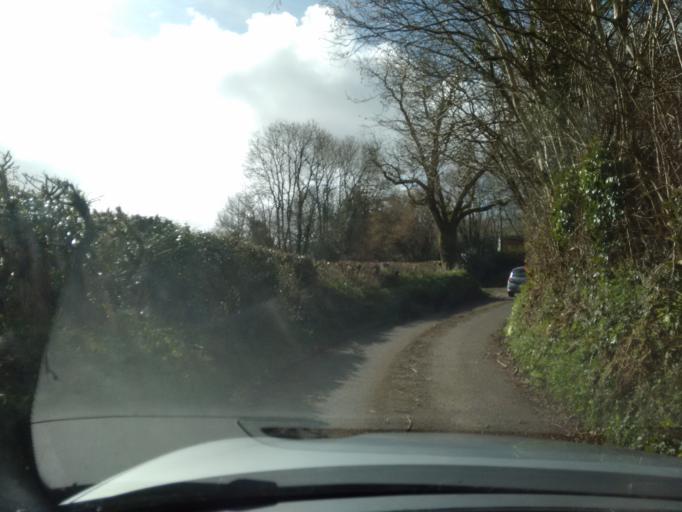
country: GB
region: England
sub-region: Cornwall
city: Launceston
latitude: 50.6007
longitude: -4.3405
